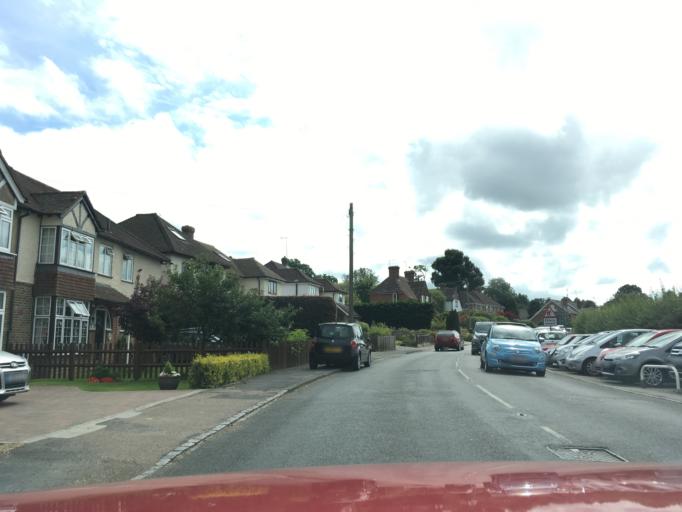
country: GB
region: England
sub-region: East Sussex
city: Crowborough
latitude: 51.1145
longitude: 0.1847
